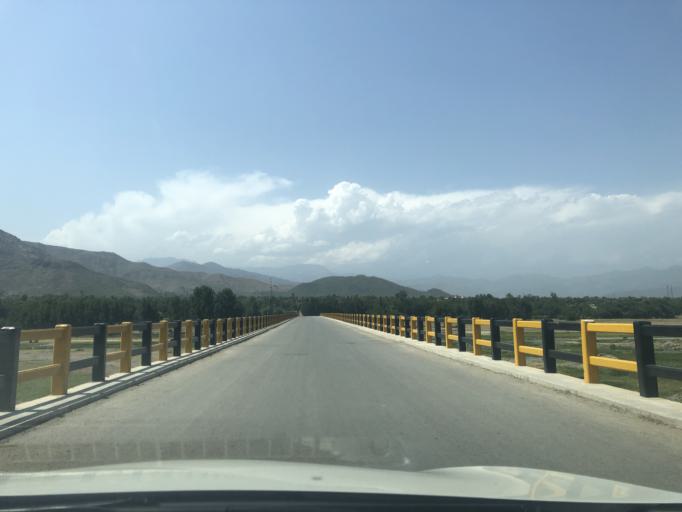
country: PK
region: Khyber Pakhtunkhwa
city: Timurgara
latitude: 34.7919
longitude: 71.6631
